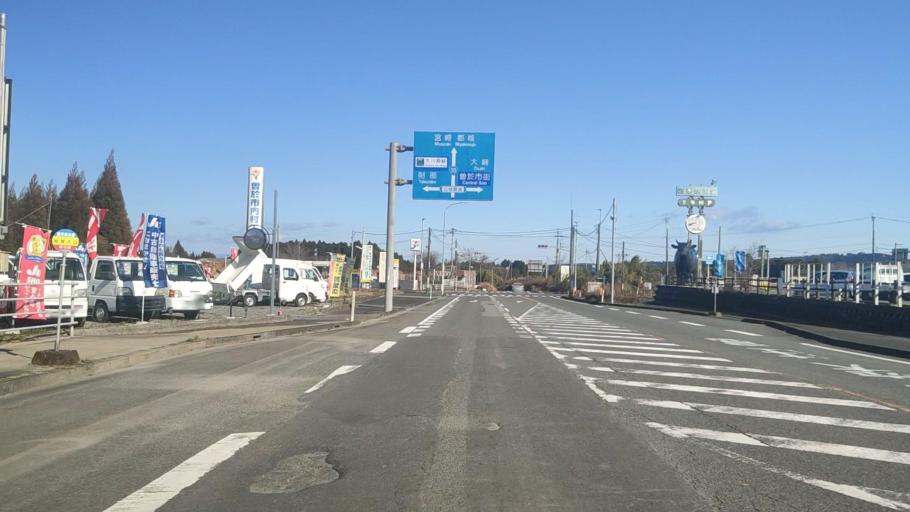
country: JP
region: Kagoshima
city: Sueyoshicho-ninokata
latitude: 31.6884
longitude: 130.9695
